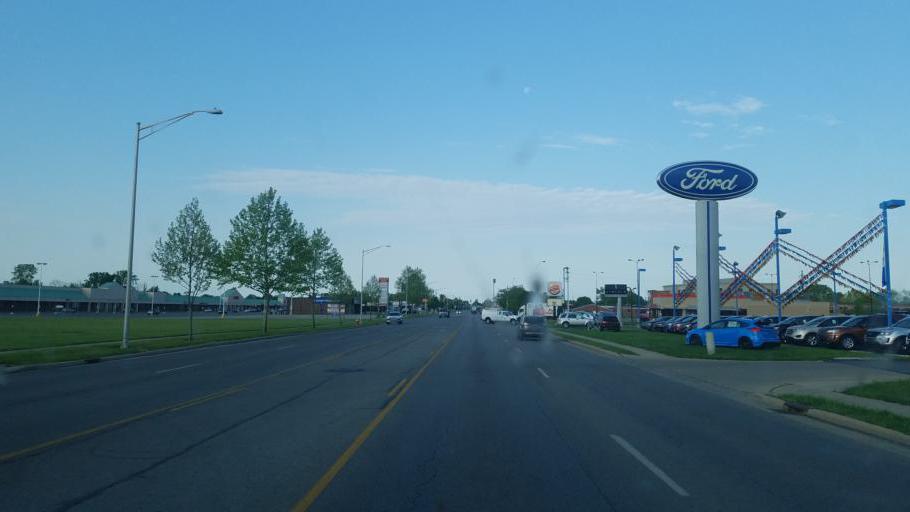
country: US
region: Ohio
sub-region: Fayette County
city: Washington Court House
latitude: 39.5504
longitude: -83.4233
